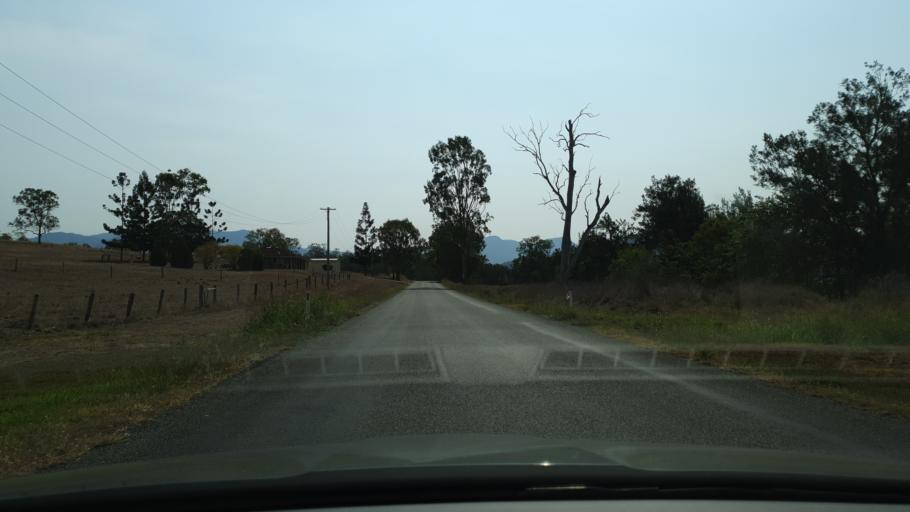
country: AU
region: Queensland
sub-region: Ipswich
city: Deebing Heights
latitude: -28.1373
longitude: 152.5916
